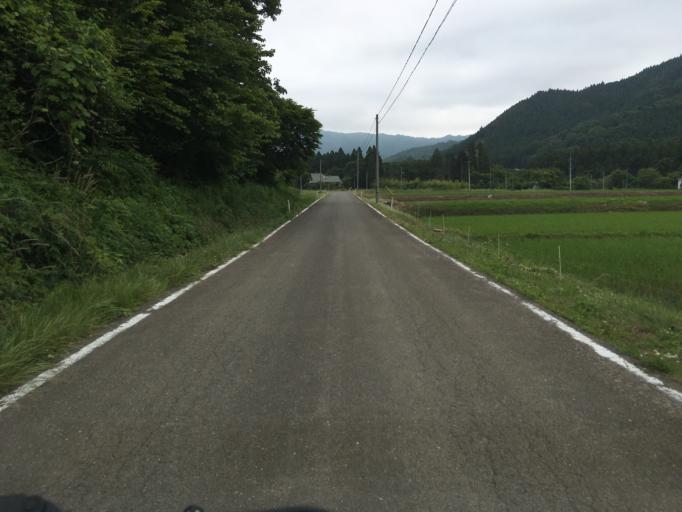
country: JP
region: Miyagi
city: Marumori
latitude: 37.7694
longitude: 140.8407
